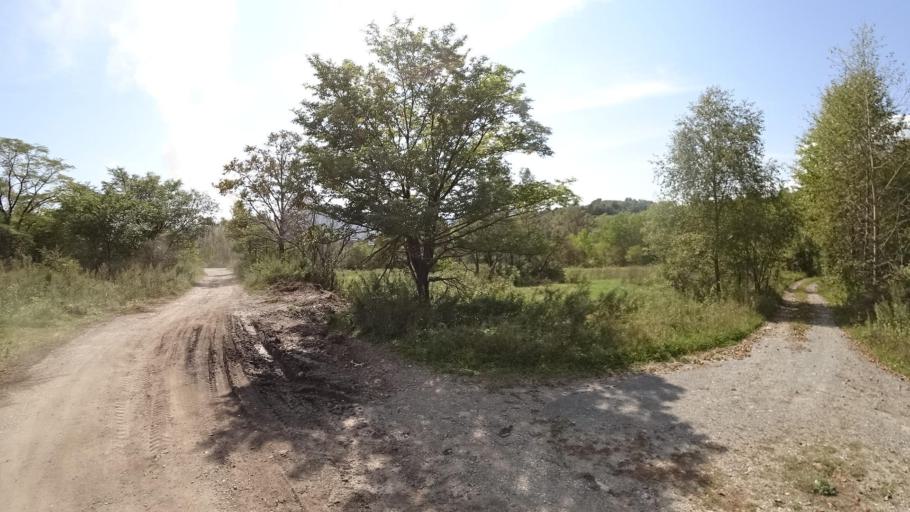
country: RU
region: Jewish Autonomous Oblast
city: Londoko
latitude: 49.0118
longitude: 131.8969
